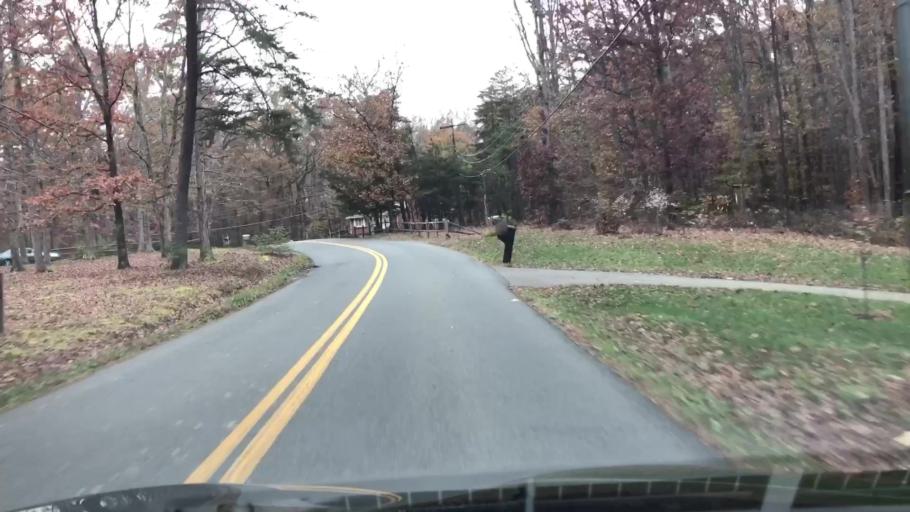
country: US
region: Virginia
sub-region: Stafford County
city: Falmouth
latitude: 38.3994
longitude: -77.5753
